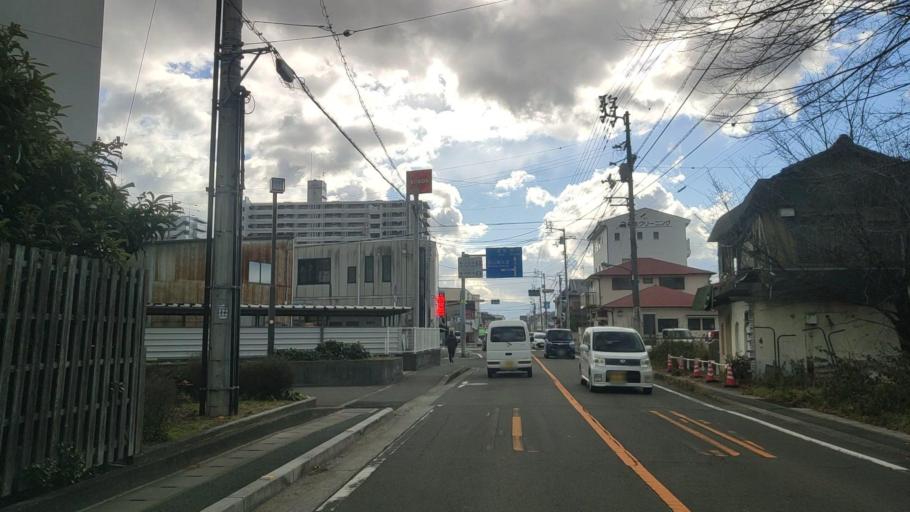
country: JP
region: Ehime
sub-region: Shikoku-chuo Shi
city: Matsuyama
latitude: 33.8683
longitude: 132.7177
